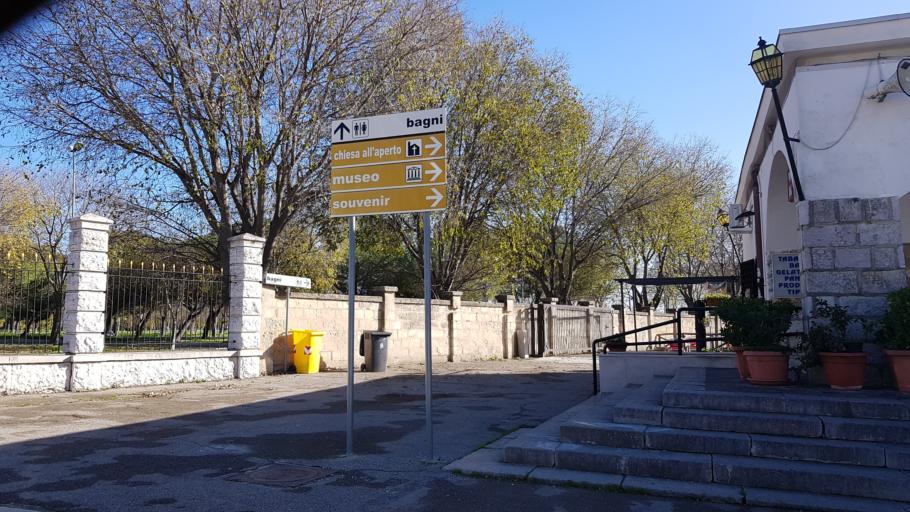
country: IT
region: Apulia
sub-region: Provincia di Foggia
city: Carapelle
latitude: 41.3825
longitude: 15.6419
